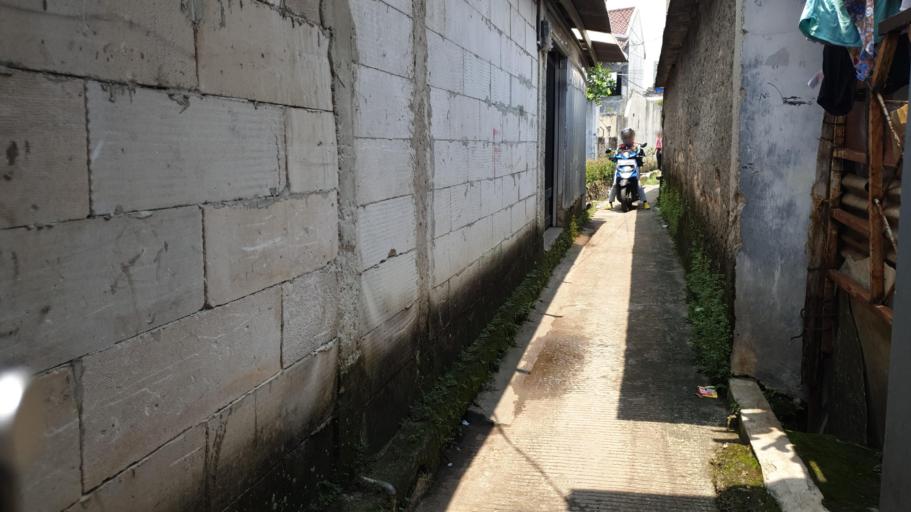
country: ID
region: West Java
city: Pamulang
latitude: -6.3013
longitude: 106.7788
